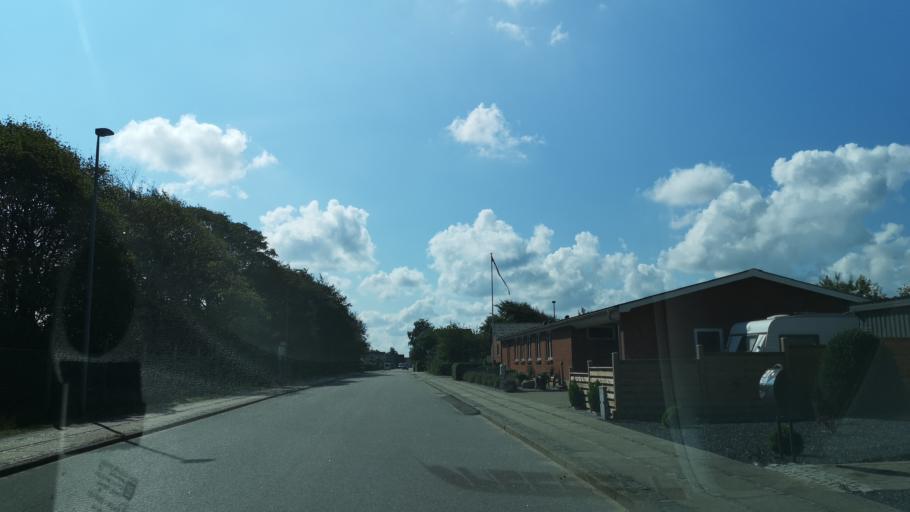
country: DK
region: Central Jutland
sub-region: Ringkobing-Skjern Kommune
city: Skjern
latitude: 55.9541
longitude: 8.4974
